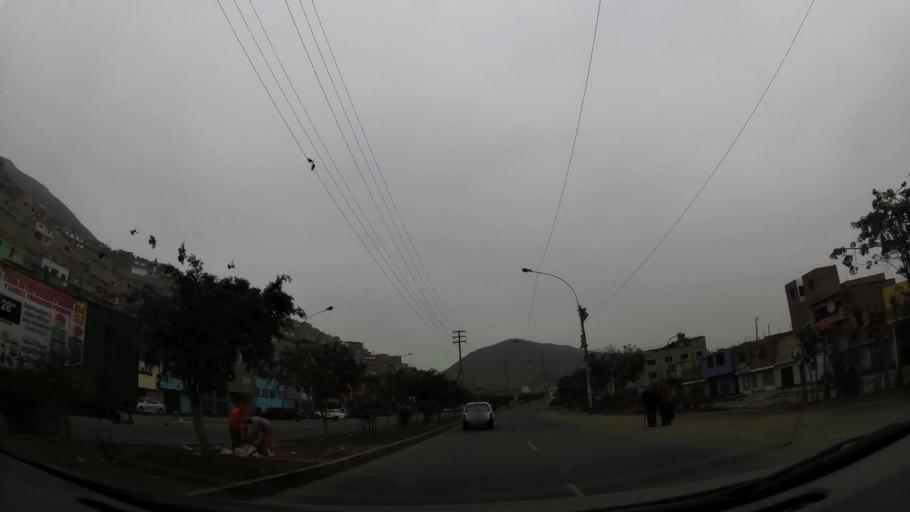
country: PE
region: Lima
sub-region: Lima
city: Urb. Santo Domingo
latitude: -11.9064
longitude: -77.0319
